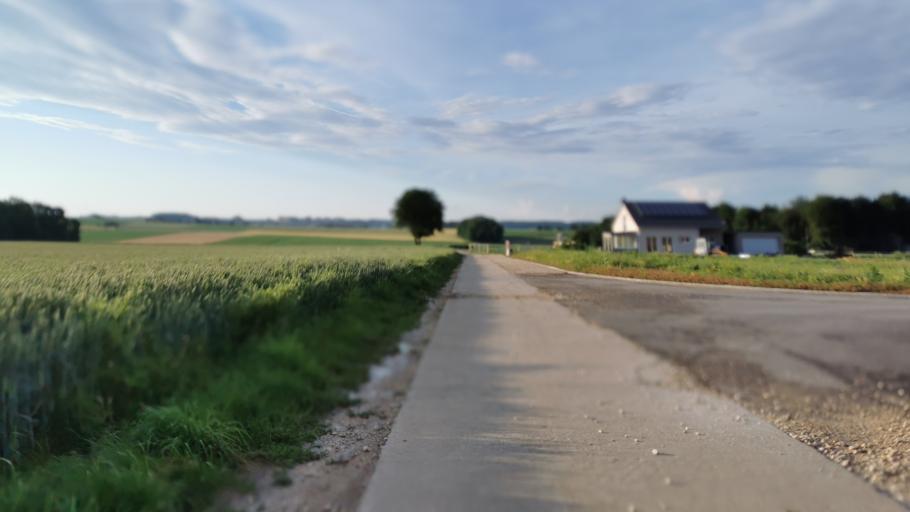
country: DE
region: Bavaria
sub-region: Swabia
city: Wallerstein
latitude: 48.8941
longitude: 10.4724
